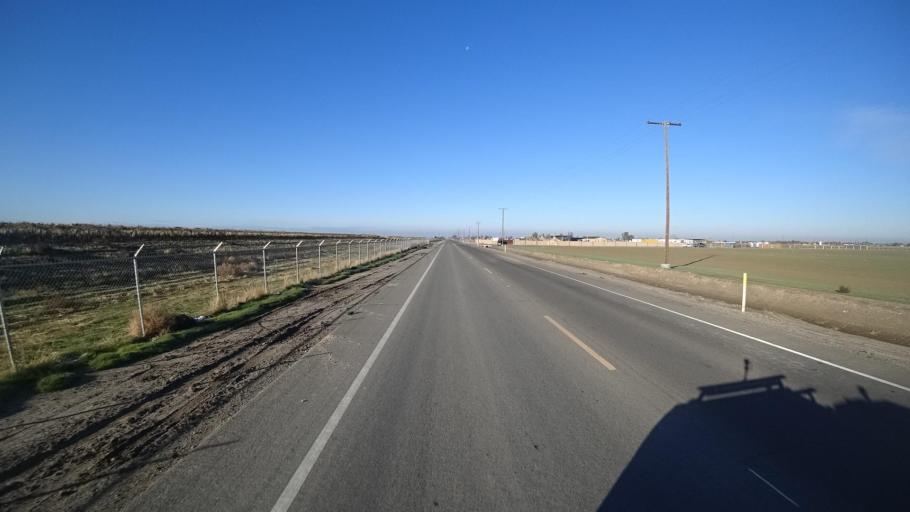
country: US
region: California
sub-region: Kern County
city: Delano
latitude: 35.7759
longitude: -119.2882
